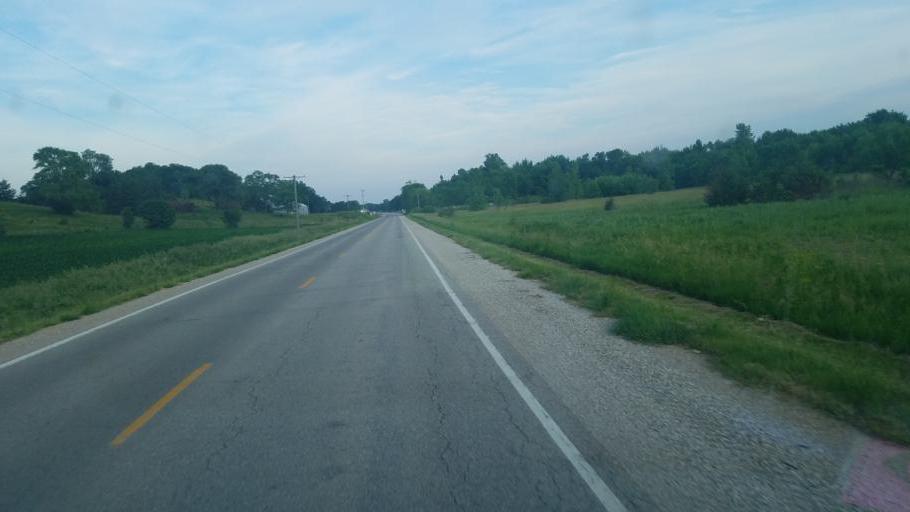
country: US
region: Iowa
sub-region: Benton County
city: Belle Plaine
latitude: 41.9314
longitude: -92.3981
